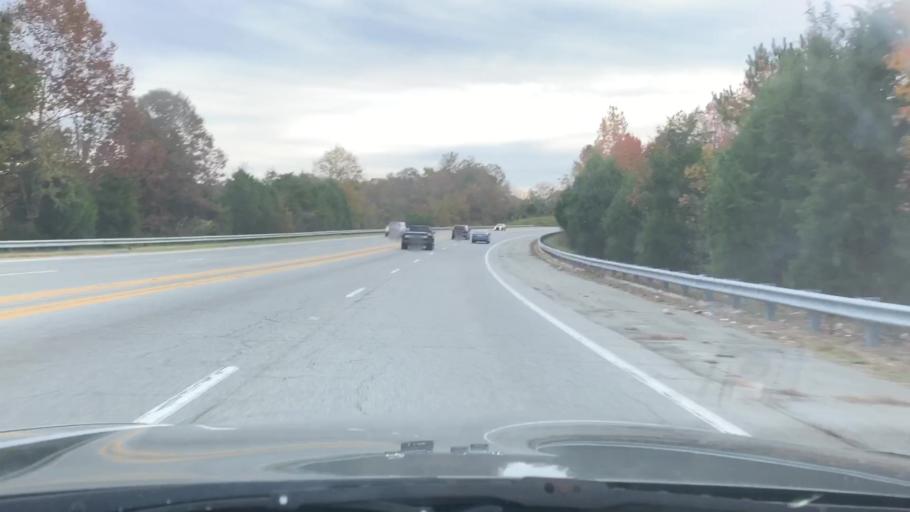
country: US
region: North Carolina
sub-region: Alamance County
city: Haw River
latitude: 36.0976
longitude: -79.3656
